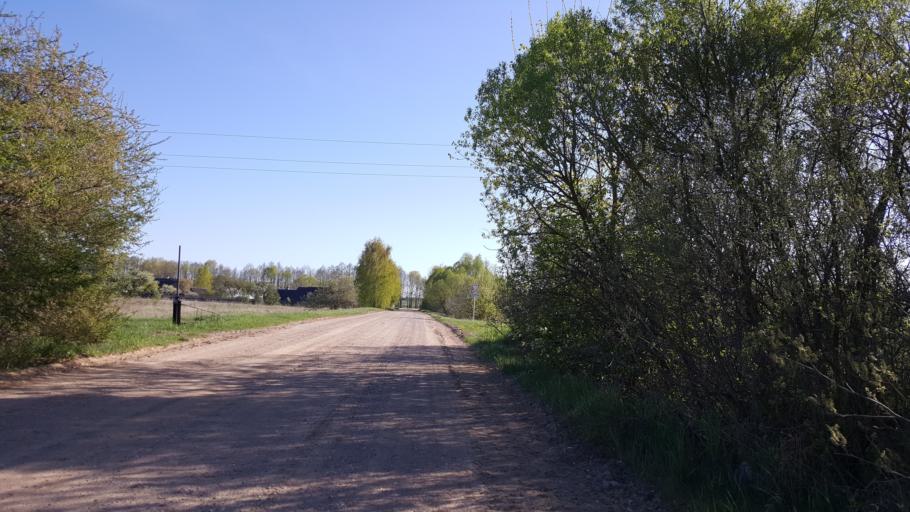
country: BY
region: Brest
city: Kamyanyets
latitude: 52.4247
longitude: 23.8794
